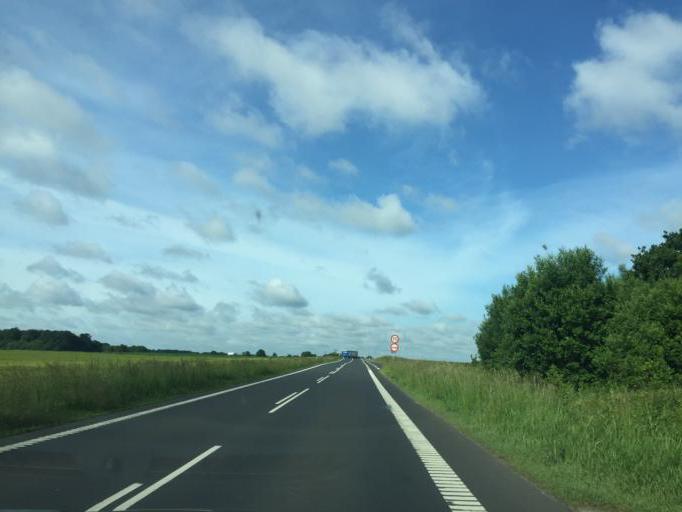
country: DK
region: South Denmark
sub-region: Fredericia Kommune
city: Snoghoj
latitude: 55.5352
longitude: 9.6742
